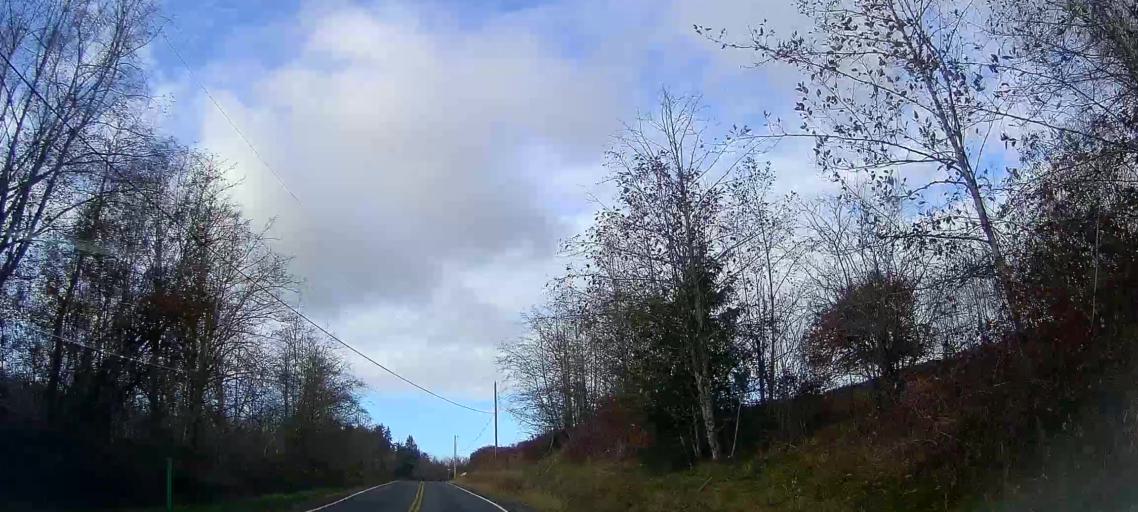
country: US
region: Washington
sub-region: Skagit County
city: Big Lake
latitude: 48.4101
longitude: -122.2191
